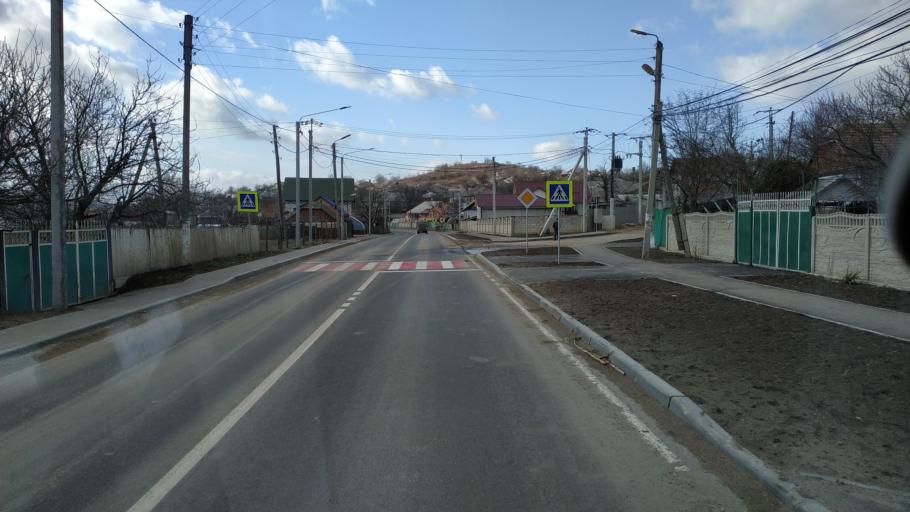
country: MD
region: Calarasi
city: Calarasi
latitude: 47.2887
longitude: 28.1948
